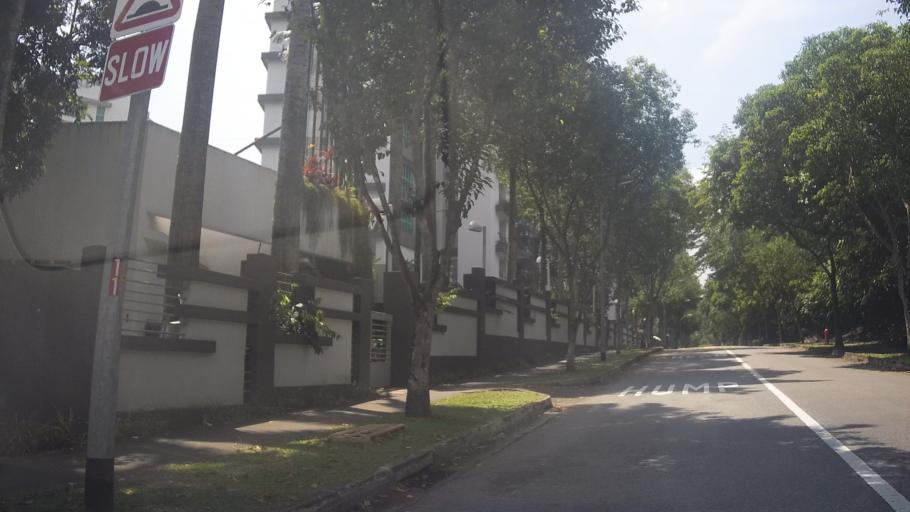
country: SG
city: Singapore
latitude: 1.3466
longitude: 103.7743
